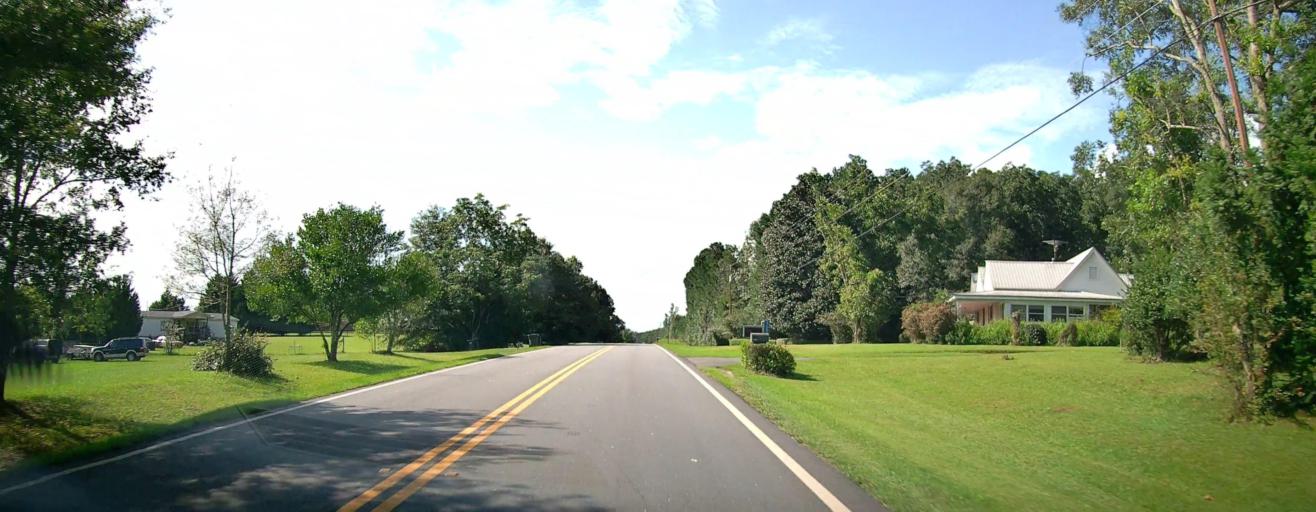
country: US
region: Georgia
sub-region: Upson County
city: Hannahs Mill
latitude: 32.9235
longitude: -84.4399
